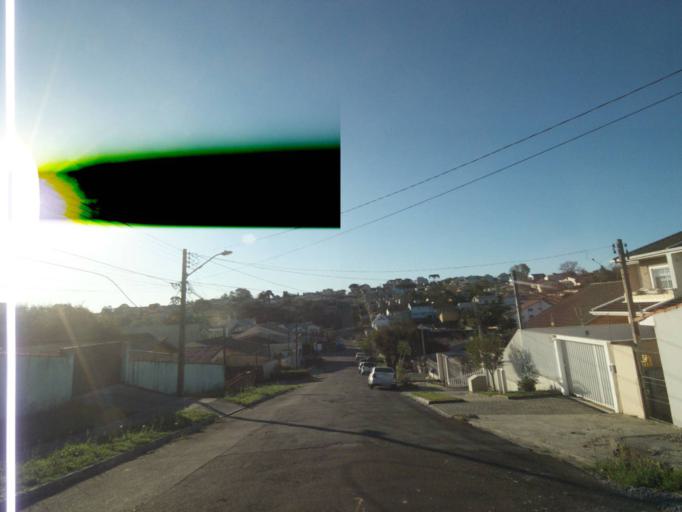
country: BR
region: Parana
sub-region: Curitiba
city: Curitiba
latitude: -25.3869
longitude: -49.2515
